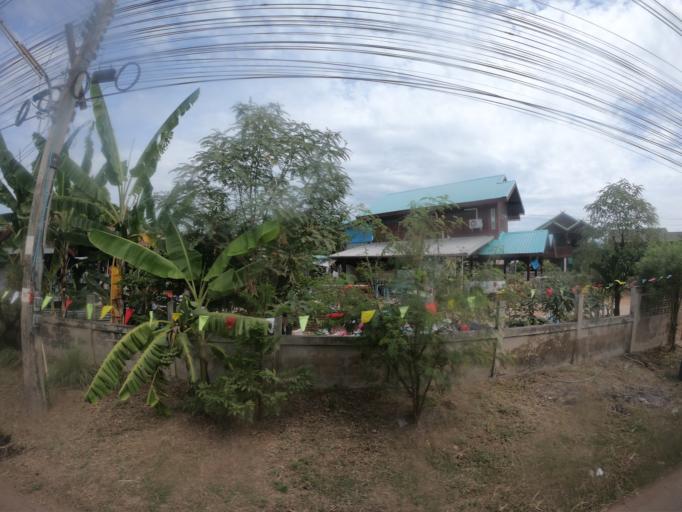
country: TH
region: Maha Sarakham
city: Chiang Yuen
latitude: 16.3498
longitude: 103.1204
